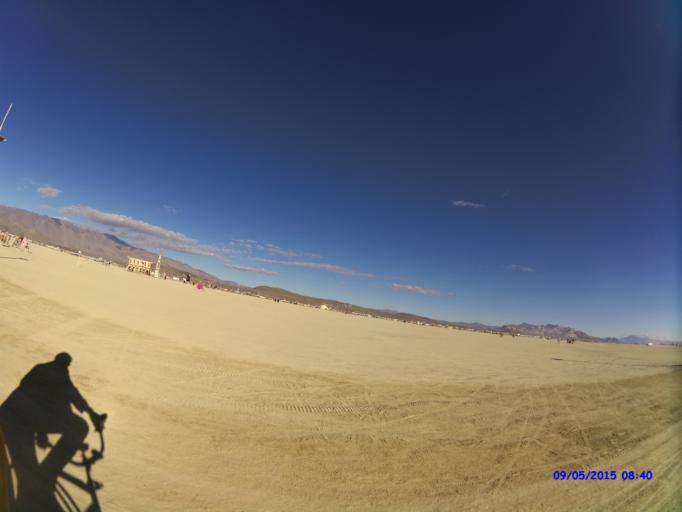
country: US
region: Nevada
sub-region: Pershing County
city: Lovelock
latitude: 40.7851
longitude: -119.2086
